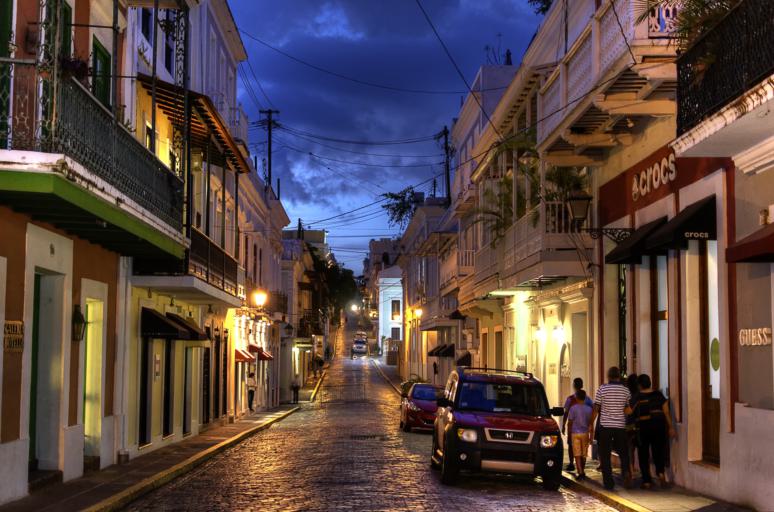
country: PR
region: San Juan
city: San Juan
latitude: 18.4645
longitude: -66.1179
